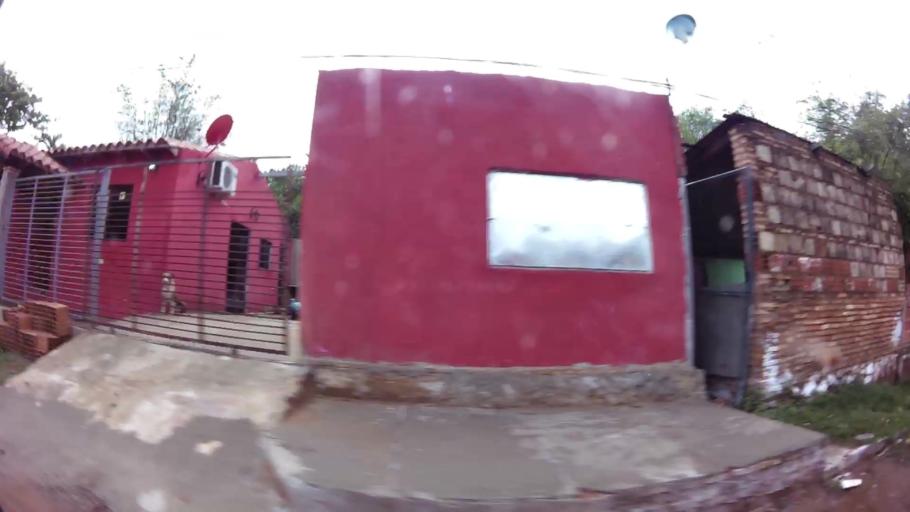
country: PY
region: Central
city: Limpio
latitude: -25.1368
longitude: -57.4721
